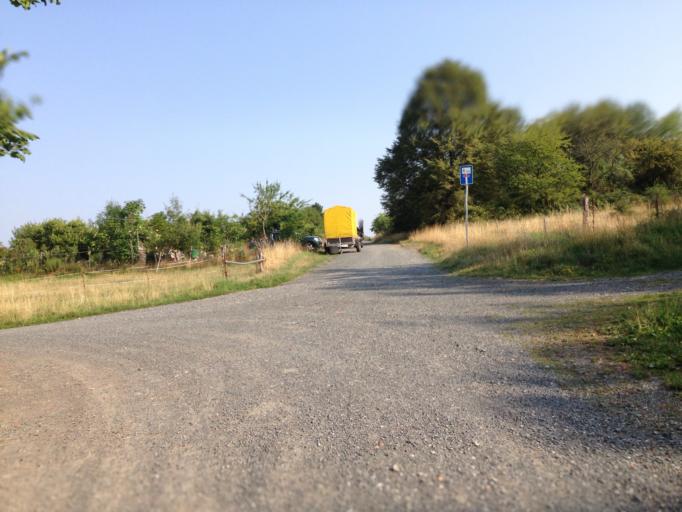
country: DE
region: Hesse
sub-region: Regierungsbezirk Giessen
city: Giessen
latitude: 50.6106
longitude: 8.6964
